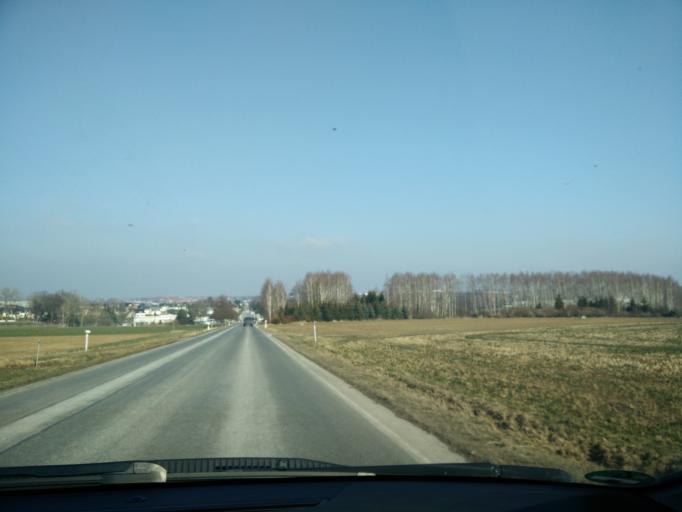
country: DE
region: Saxony
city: Hartmannsdorf
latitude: 50.8804
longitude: 12.7857
